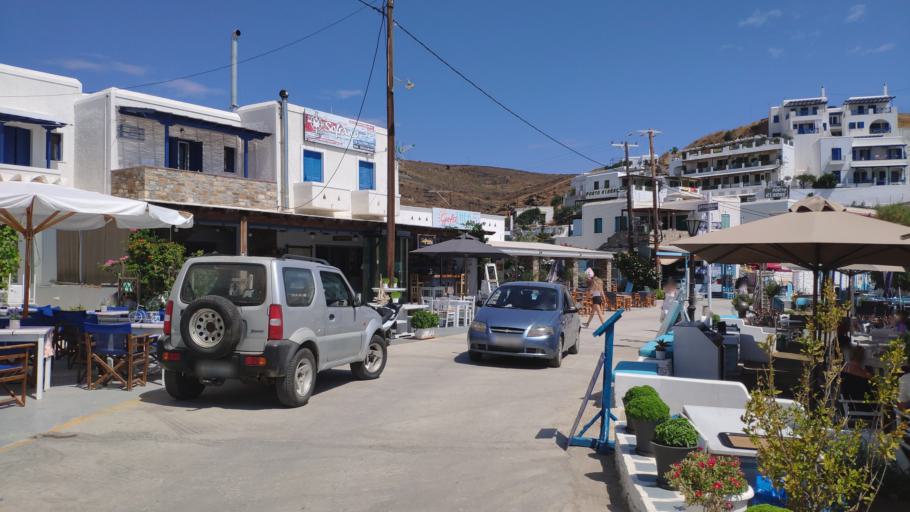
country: GR
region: South Aegean
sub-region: Nomos Kykladon
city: Kythnos
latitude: 37.4426
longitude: 24.4251
